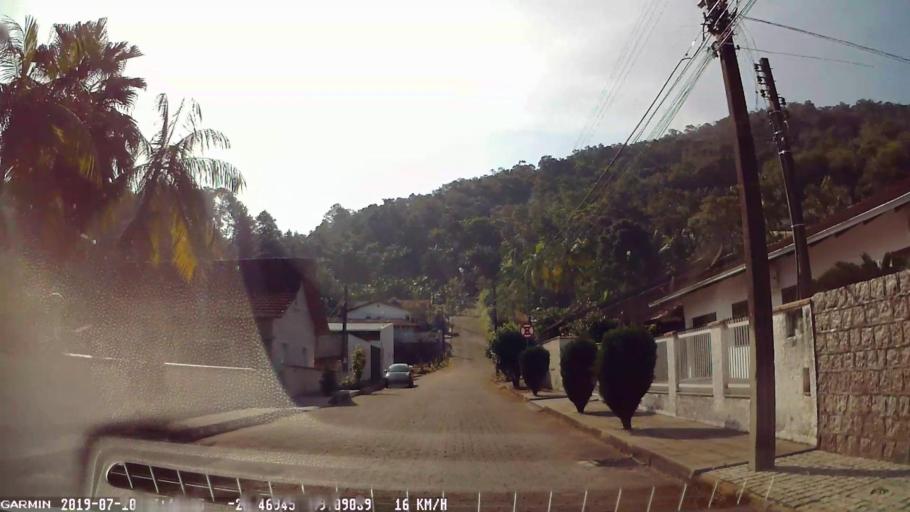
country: BR
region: Santa Catarina
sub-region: Jaragua Do Sul
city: Jaragua do Sul
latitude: -26.4694
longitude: -49.0904
